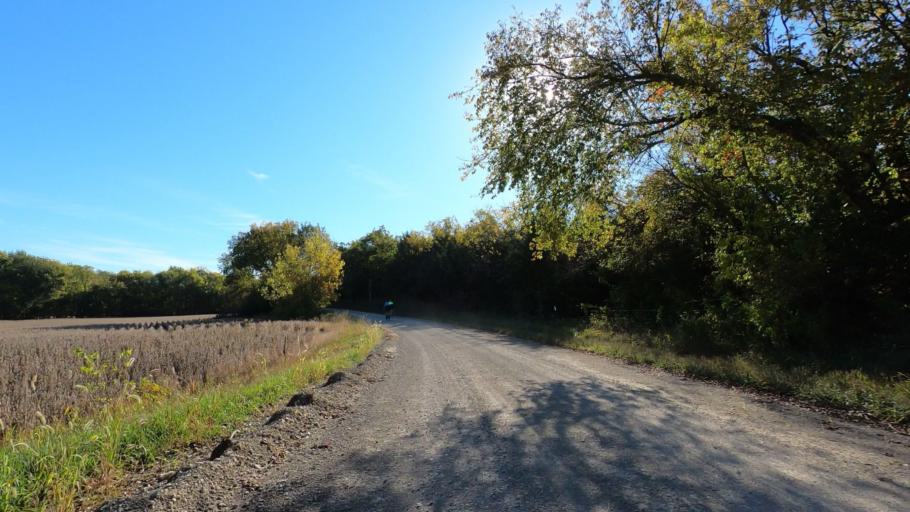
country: US
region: Kansas
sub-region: Marshall County
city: Blue Rapids
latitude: 39.4898
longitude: -96.6118
